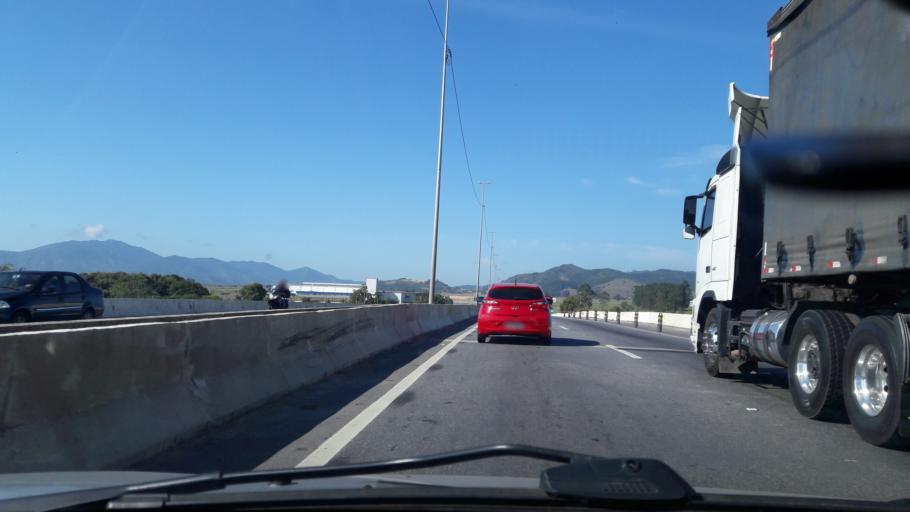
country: BR
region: Santa Catarina
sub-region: Tijucas
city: Tijucas
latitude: -27.2422
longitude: -48.6308
